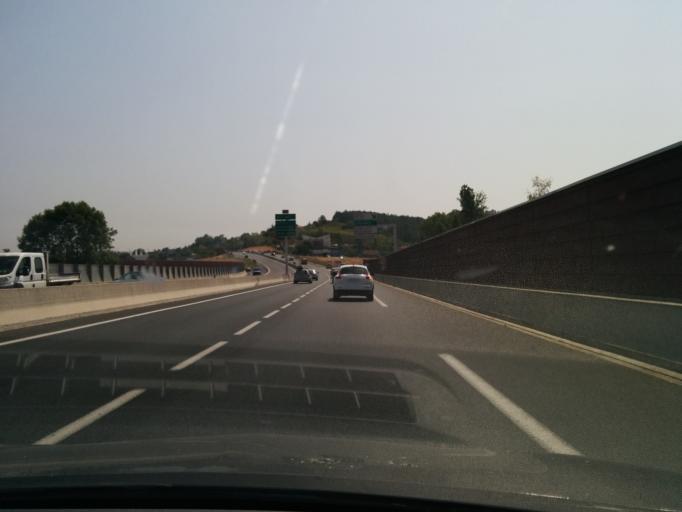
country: FR
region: Midi-Pyrenees
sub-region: Departement du Tarn
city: Le Sequestre
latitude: 43.9110
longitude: 2.1362
